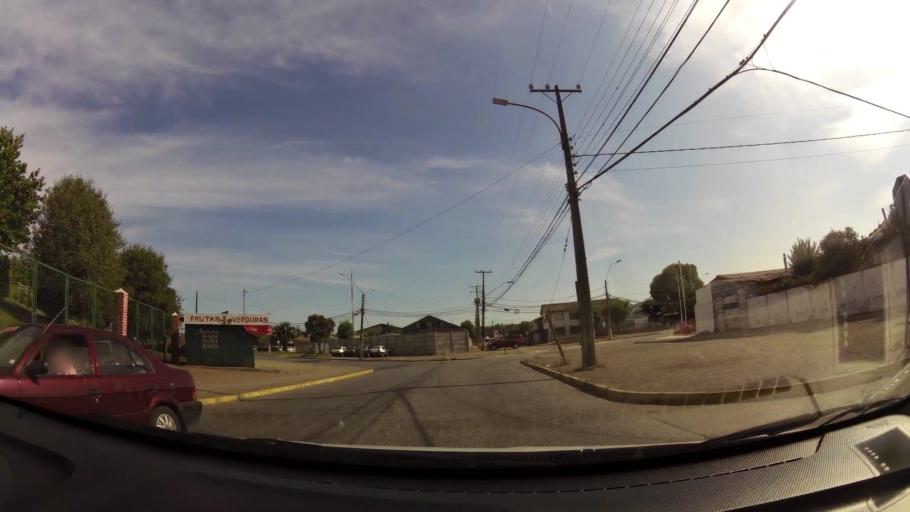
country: CL
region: Biobio
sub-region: Provincia de Concepcion
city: Talcahuano
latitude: -36.7839
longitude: -73.1017
